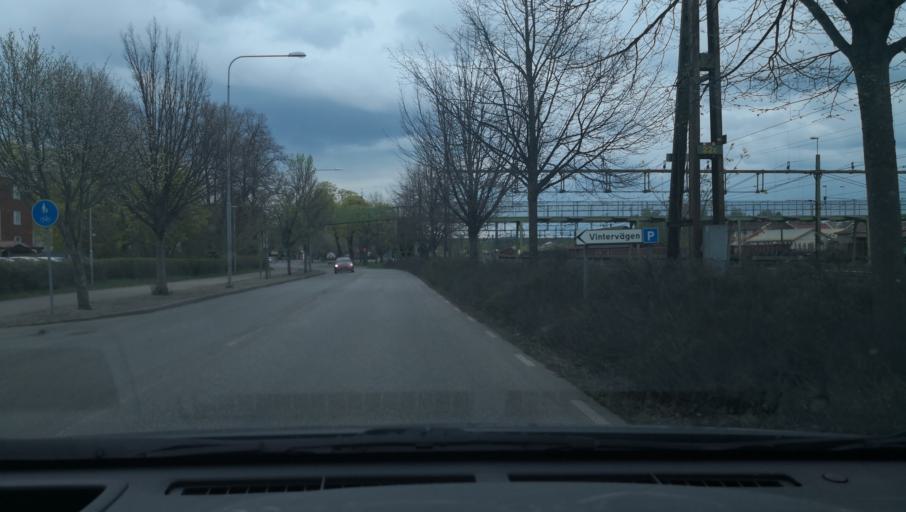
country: SE
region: Dalarna
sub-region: Avesta Kommun
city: Avesta
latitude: 60.1318
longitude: 16.2154
